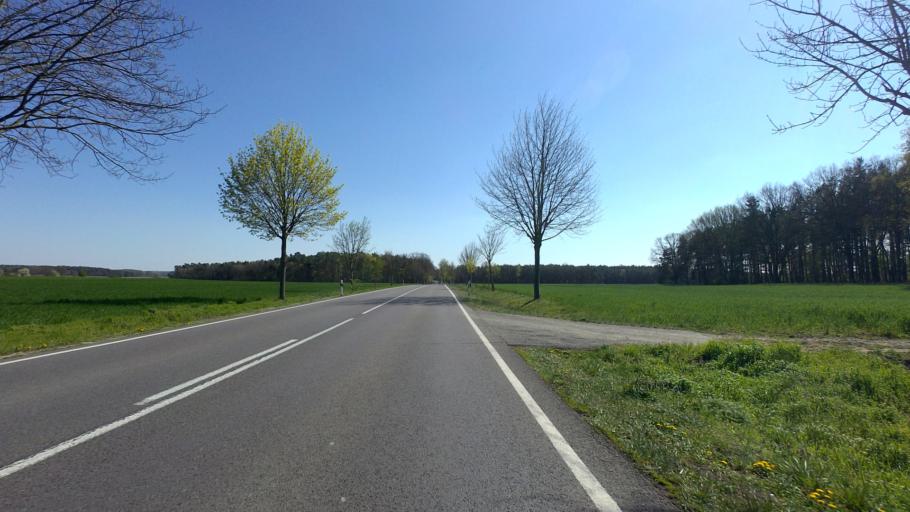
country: DE
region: Saxony-Anhalt
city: Pretzier
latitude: 52.7117
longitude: 11.2510
